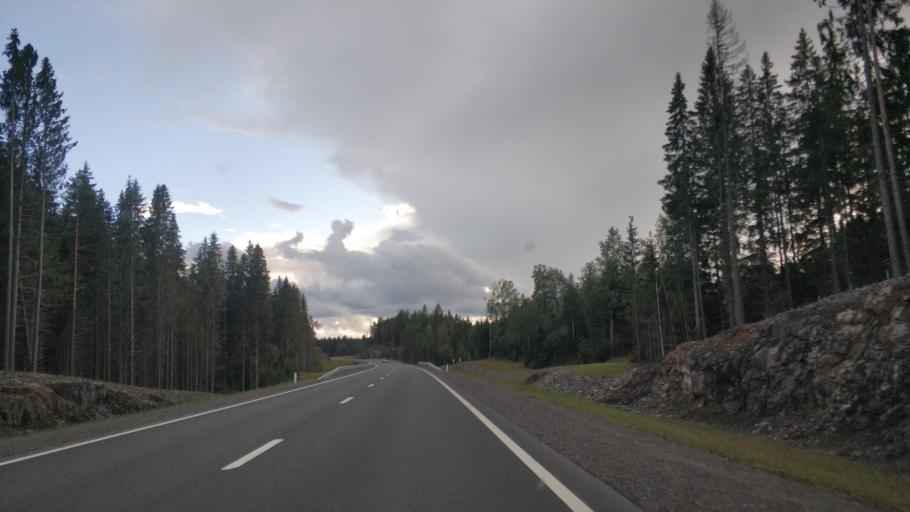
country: RU
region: Republic of Karelia
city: Lakhdenpokh'ya
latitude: 61.4281
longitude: 29.9690
